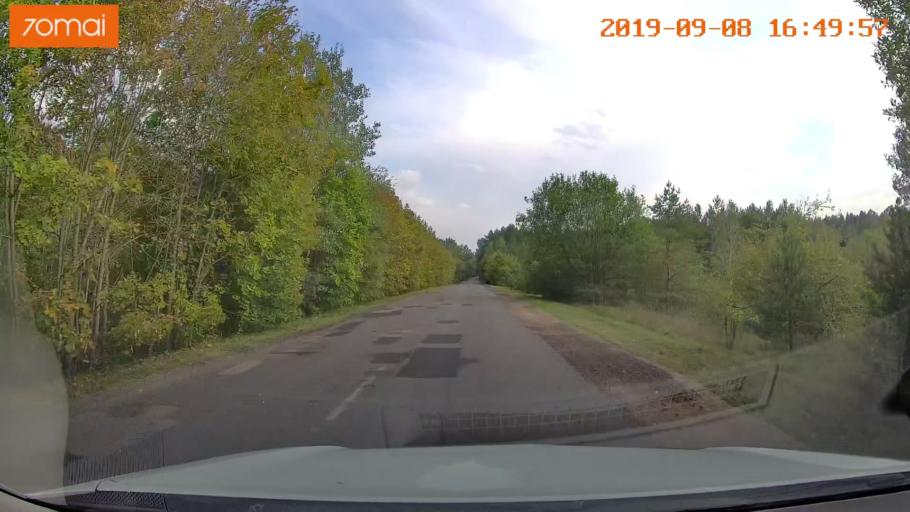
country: BY
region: Grodnenskaya
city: Hrodna
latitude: 53.8053
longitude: 23.8816
